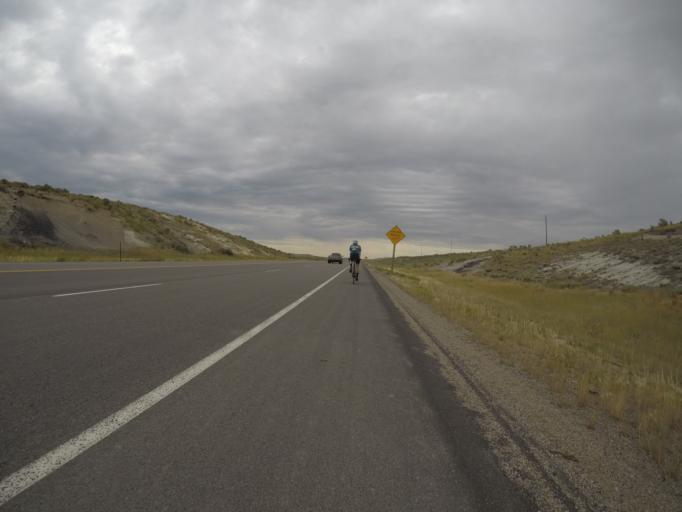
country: US
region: Wyoming
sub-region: Lincoln County
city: Kemmerer
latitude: 41.8040
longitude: -110.6027
